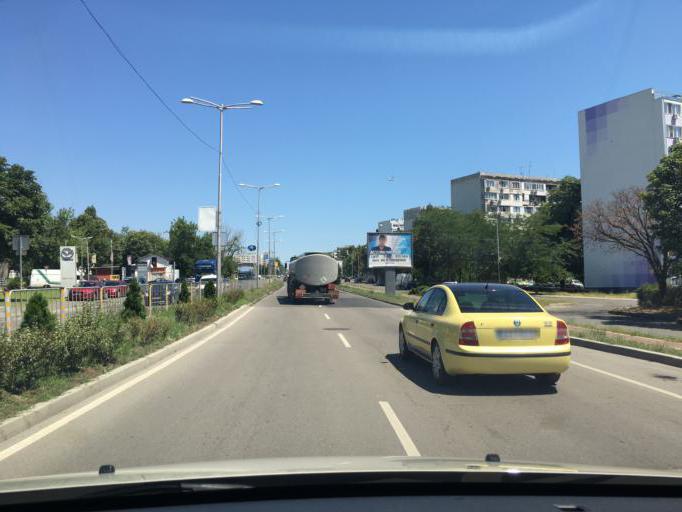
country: BG
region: Burgas
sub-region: Obshtina Burgas
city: Burgas
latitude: 42.5212
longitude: 27.4412
